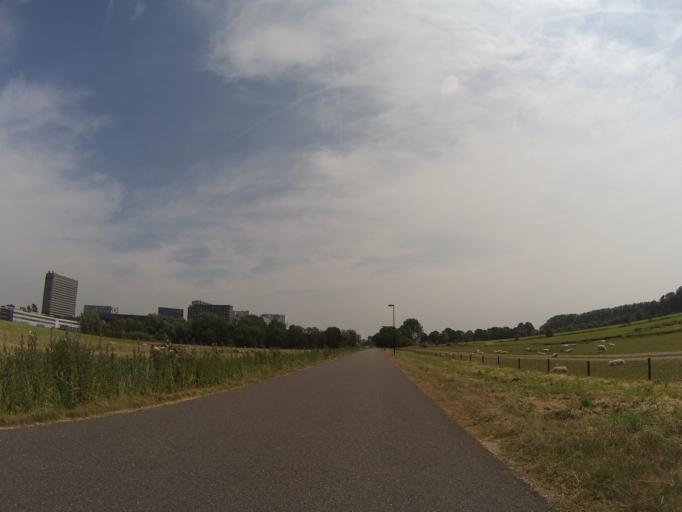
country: NL
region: Utrecht
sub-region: Gemeente De Bilt
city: De Bilt
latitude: 52.0812
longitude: 5.1675
